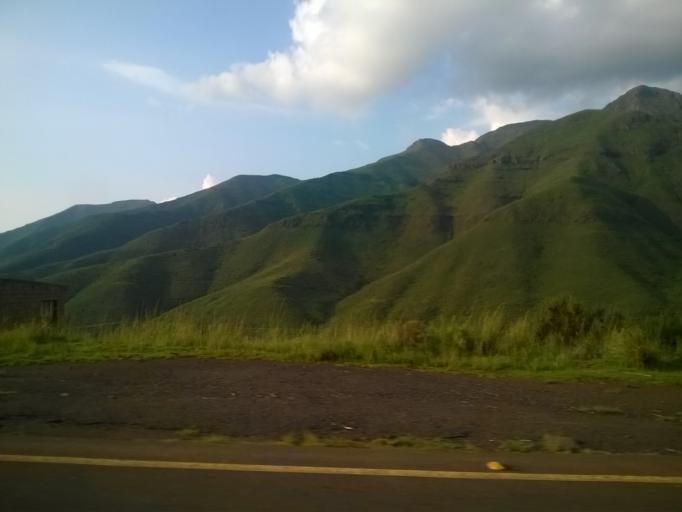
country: LS
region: Butha-Buthe
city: Butha-Buthe
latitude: -29.0509
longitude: 28.3372
